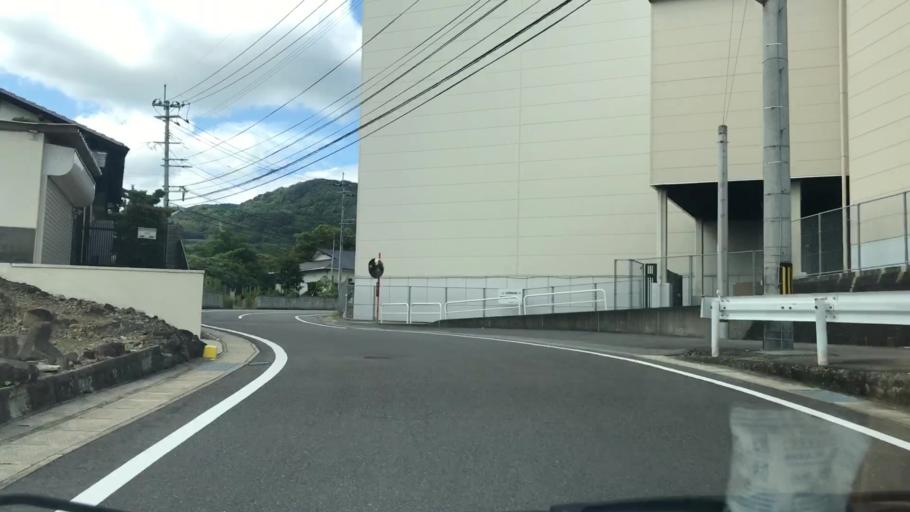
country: JP
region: Saga Prefecture
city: Takeocho-takeo
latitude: 33.2295
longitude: 130.1417
